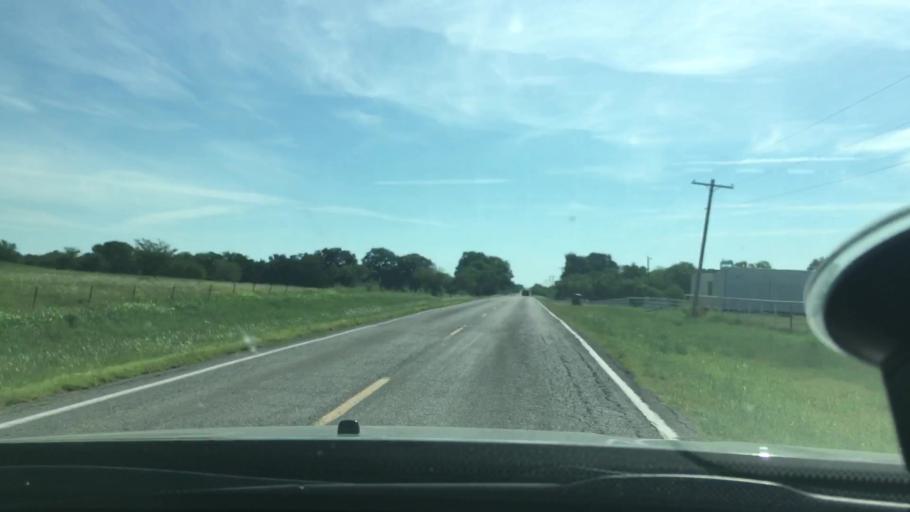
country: US
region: Oklahoma
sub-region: Carter County
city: Lone Grove
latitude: 34.3327
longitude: -97.2071
